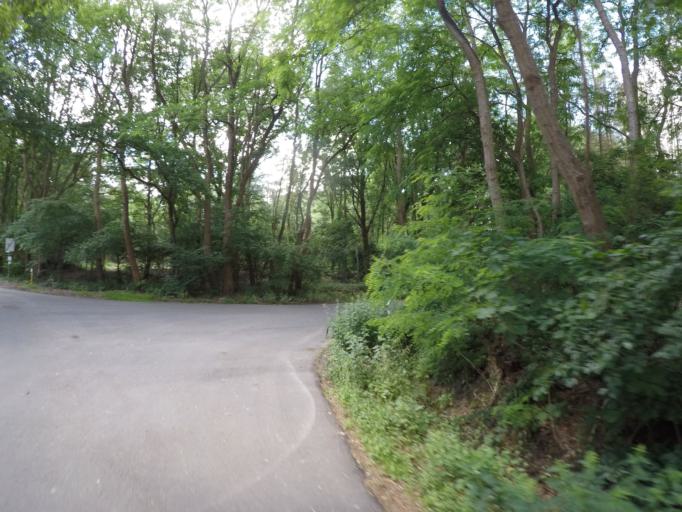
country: BE
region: Flanders
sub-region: Provincie Antwerpen
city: Vosselaar
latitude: 51.3269
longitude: 4.8880
